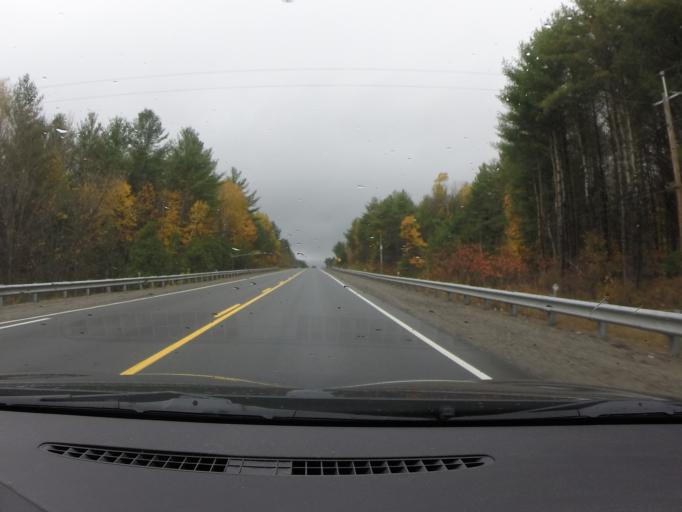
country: CA
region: Ontario
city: Belleville
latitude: 44.5474
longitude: -77.3336
